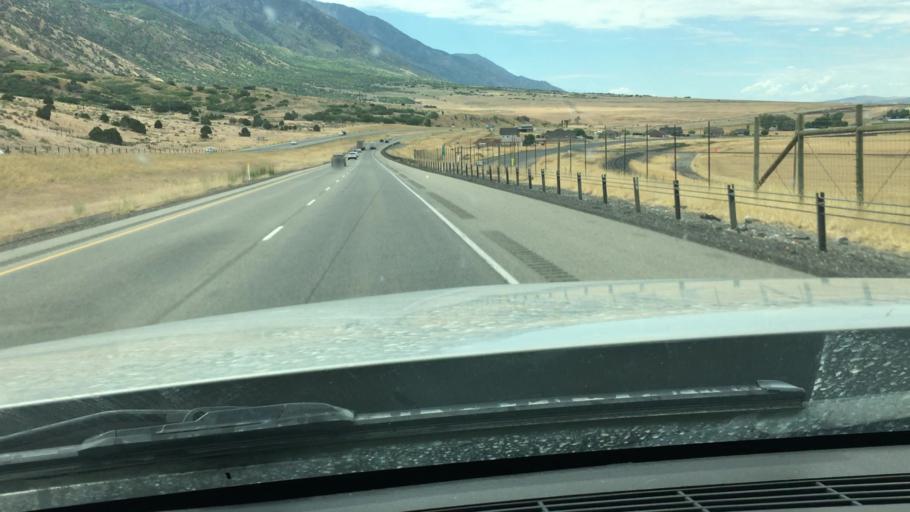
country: US
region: Utah
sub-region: Utah County
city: Santaquin
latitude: 39.9320
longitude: -111.8118
